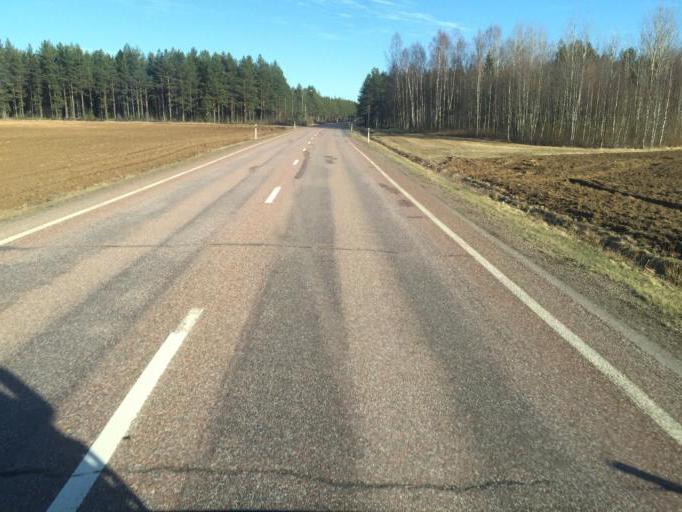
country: SE
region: Dalarna
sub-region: Vansbro Kommun
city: Jarna
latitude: 60.5410
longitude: 14.4153
